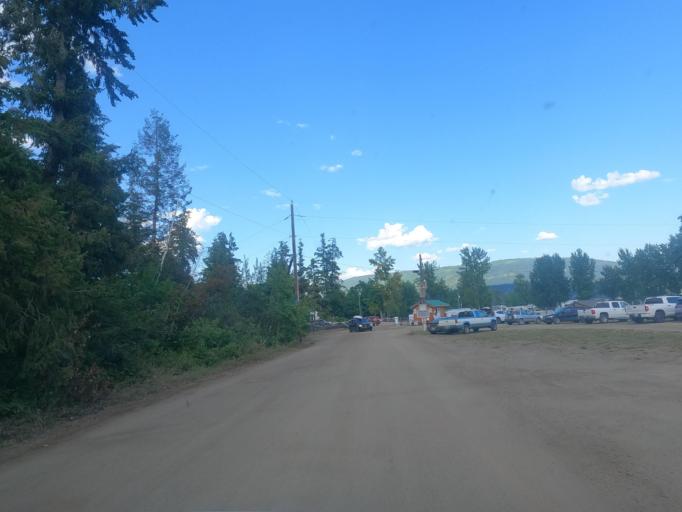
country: CA
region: British Columbia
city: Salmon Arm
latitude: 50.7303
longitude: -119.3107
